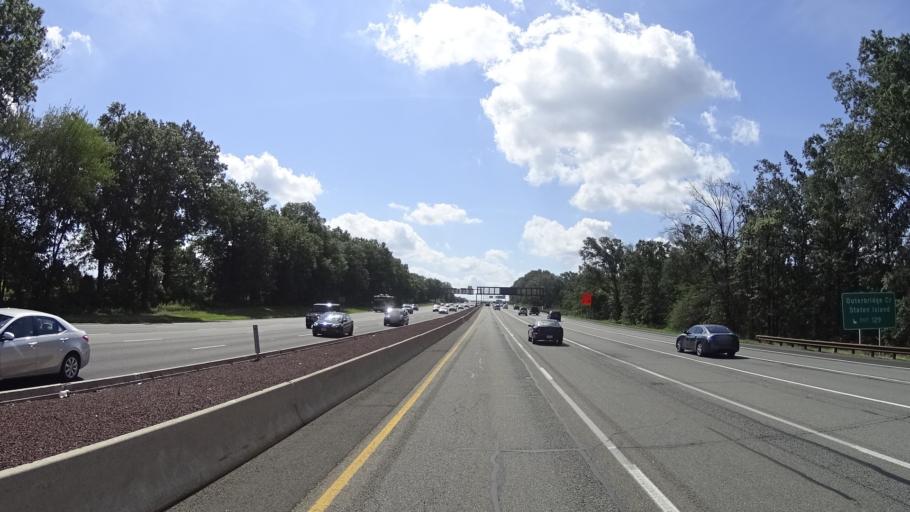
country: US
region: New Jersey
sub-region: Middlesex County
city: Fords
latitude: 40.5495
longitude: -74.3151
